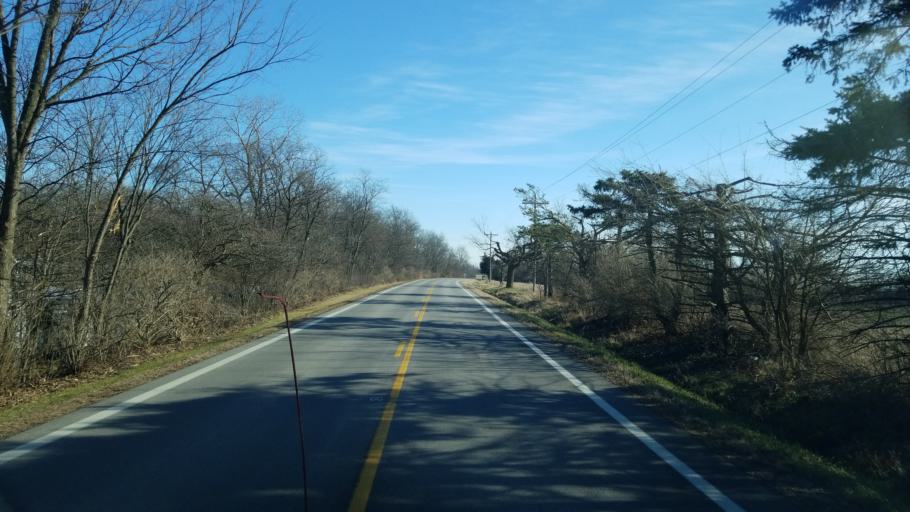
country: US
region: Ohio
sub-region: Henry County
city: Liberty Center
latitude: 41.4130
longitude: -83.8959
